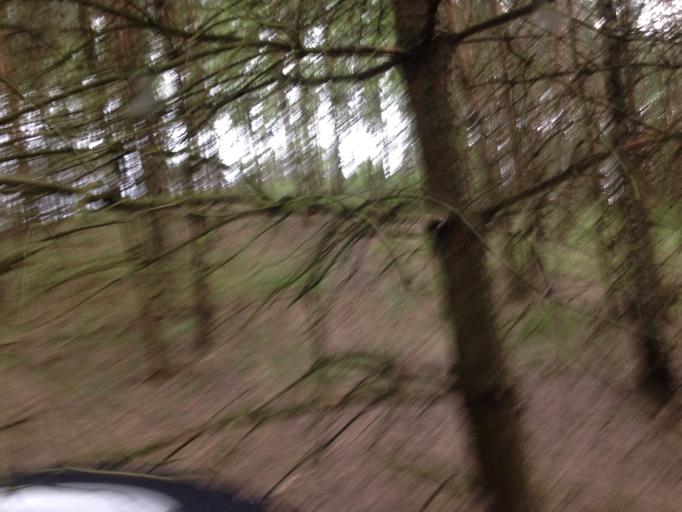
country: PL
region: Kujawsko-Pomorskie
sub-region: Powiat brodnicki
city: Bartniczka
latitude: 53.2802
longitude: 19.6598
